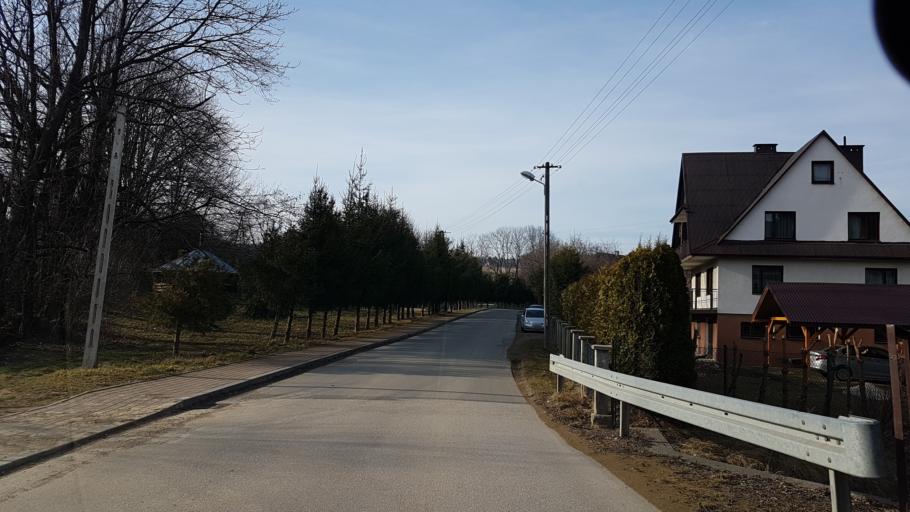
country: PL
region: Lesser Poland Voivodeship
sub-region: Powiat nowosadecki
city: Stary Sacz
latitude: 49.5454
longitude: 20.6269
